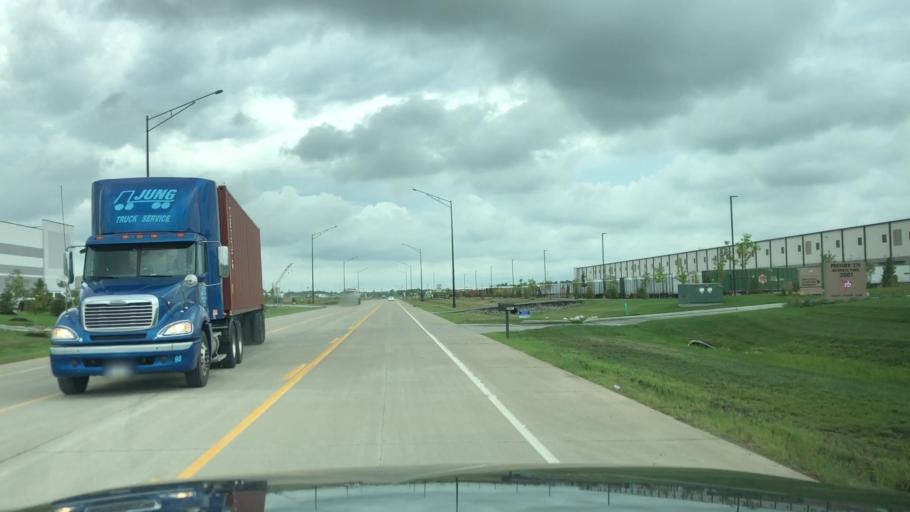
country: US
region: Missouri
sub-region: Saint Charles County
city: Saint Peters
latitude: 38.8125
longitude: -90.5644
